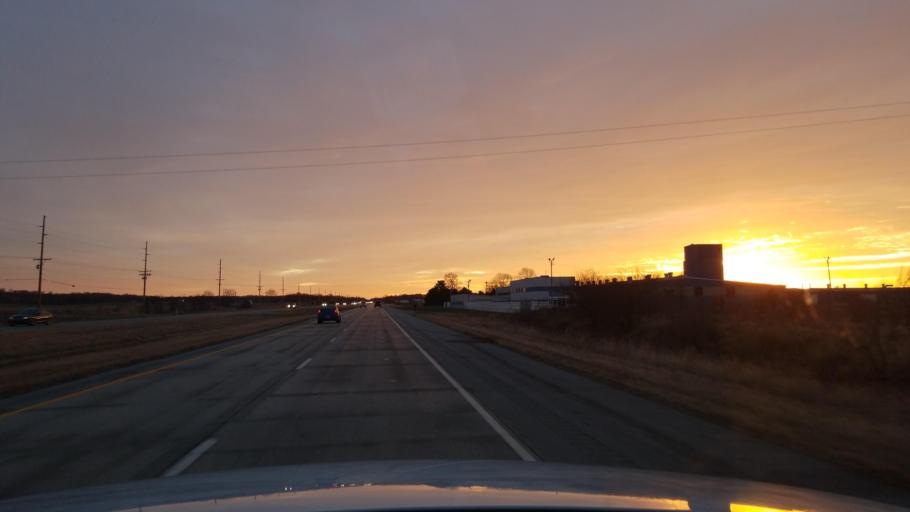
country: US
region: Indiana
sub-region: Posey County
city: Mount Vernon
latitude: 37.9421
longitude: -87.7866
